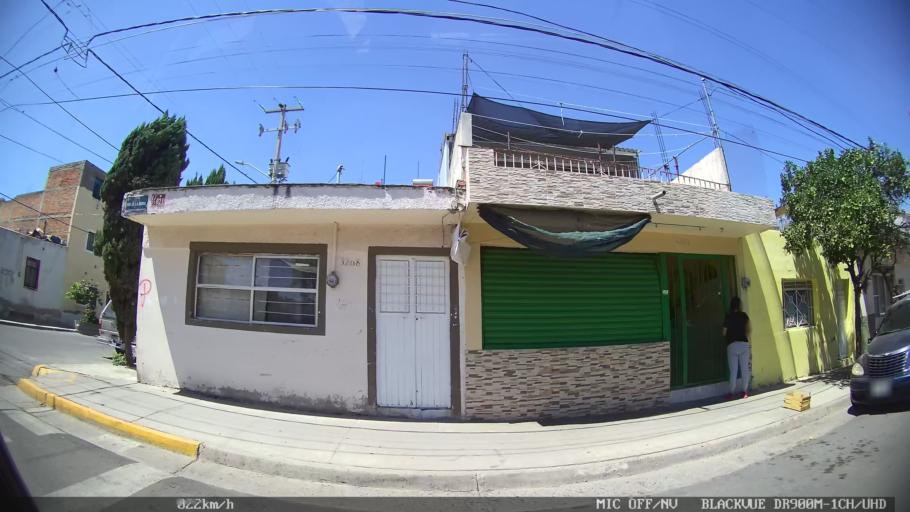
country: MX
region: Jalisco
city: Tlaquepaque
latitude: 20.6892
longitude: -103.2843
